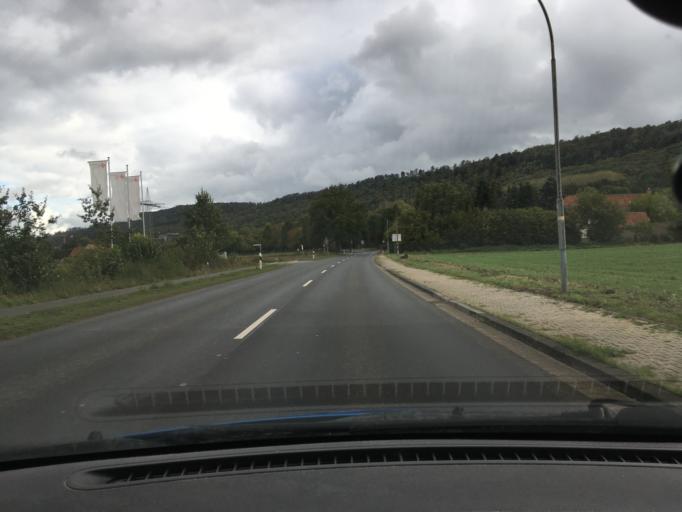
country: DE
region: Lower Saxony
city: Springe
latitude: 52.2005
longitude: 9.5570
